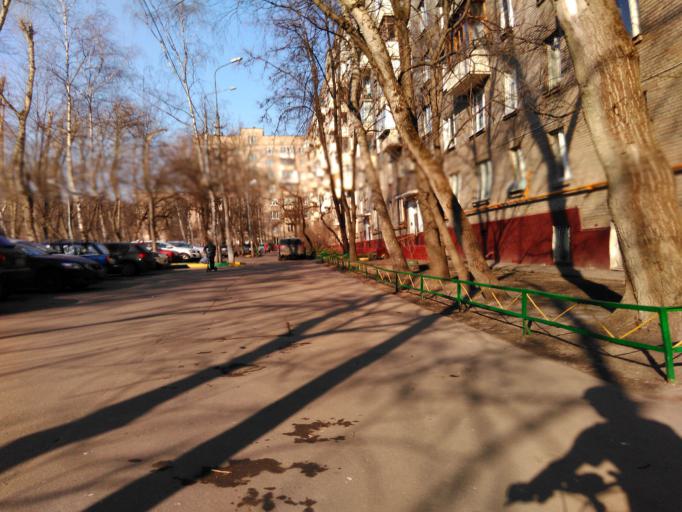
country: RU
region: Moscow
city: Ramenki
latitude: 55.7078
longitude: 37.5130
